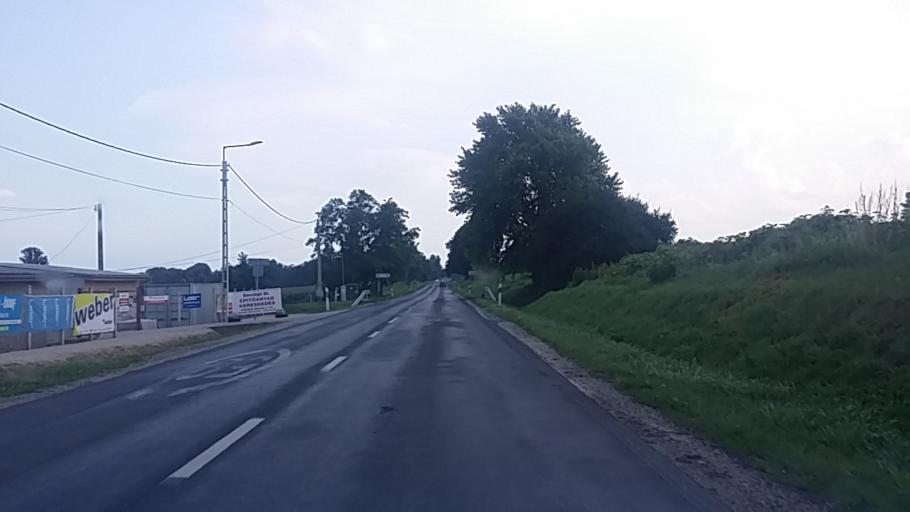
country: HU
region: Zala
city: Sarmellek
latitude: 46.7507
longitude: 17.1752
